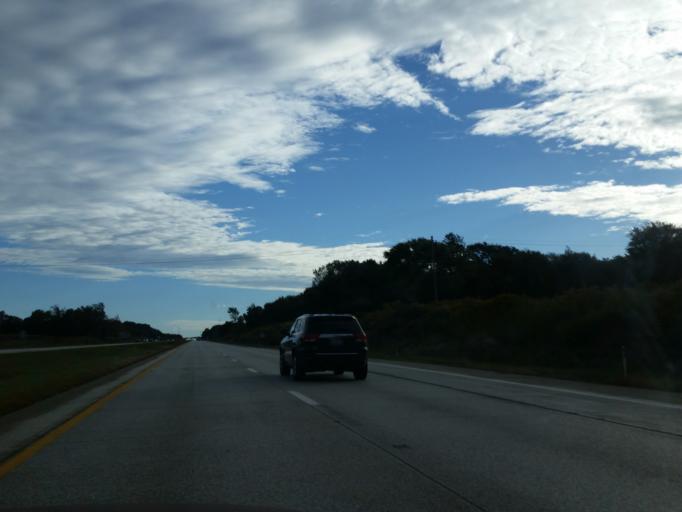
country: US
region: Pennsylvania
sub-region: Erie County
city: Northwest Harborcreek
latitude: 42.1421
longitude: -79.9175
